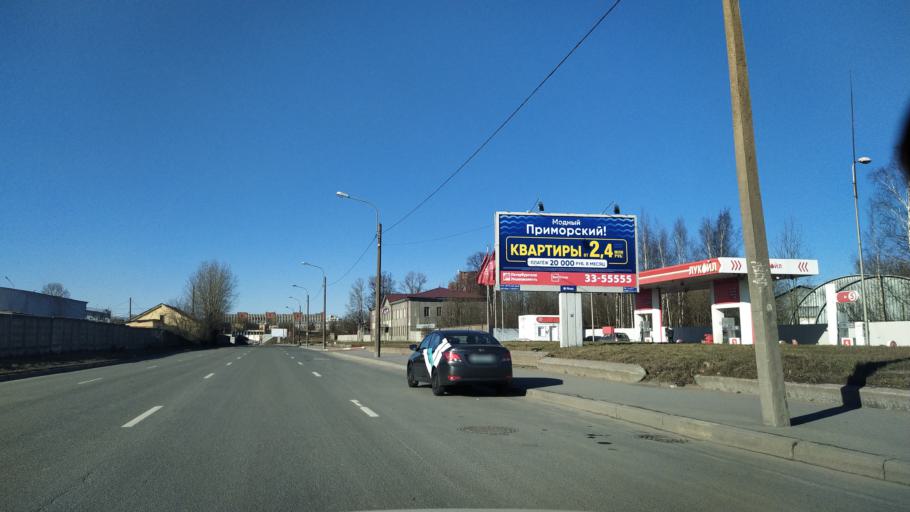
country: RU
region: St.-Petersburg
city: Centralniy
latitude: 59.9092
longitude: 30.3765
